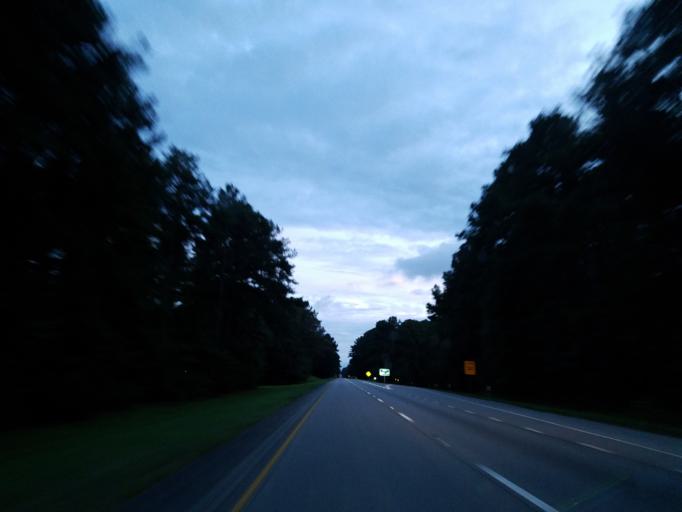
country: US
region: Mississippi
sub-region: Clarke County
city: Stonewall
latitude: 32.1674
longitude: -88.8674
